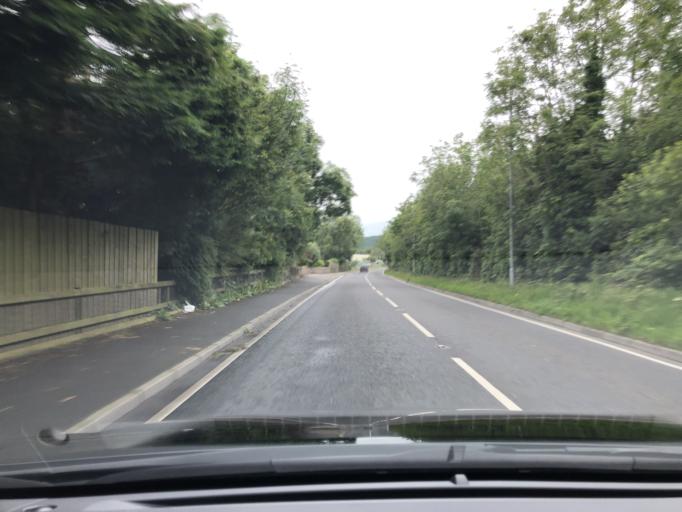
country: GB
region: Northern Ireland
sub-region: Down District
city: Castlewellan
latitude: 54.2556
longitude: -5.9511
